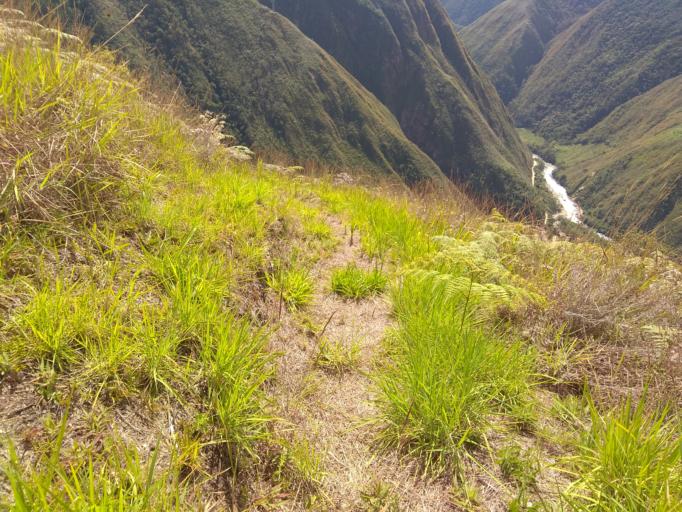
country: PE
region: Junin
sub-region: Chanchamayo
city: San Ramon
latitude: -11.3116
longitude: -75.3095
